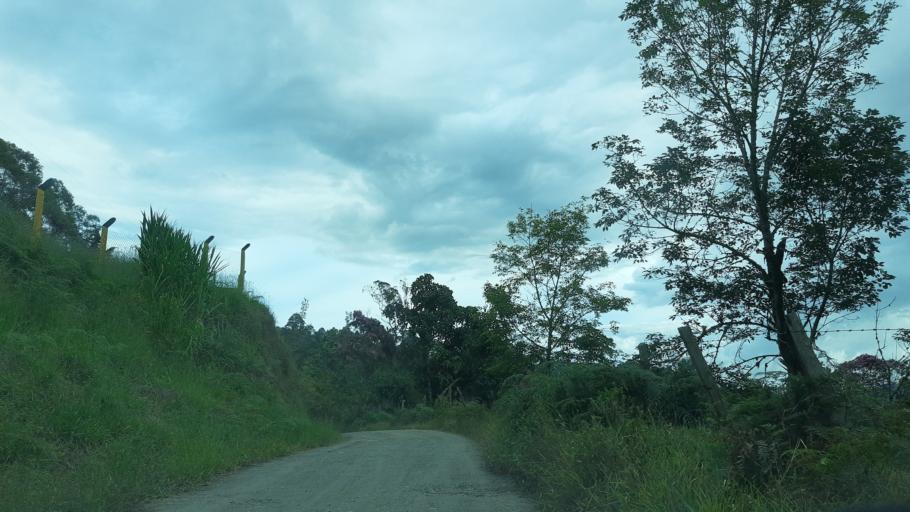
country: CO
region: Boyaca
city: Garagoa
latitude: 4.9986
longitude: -73.3303
